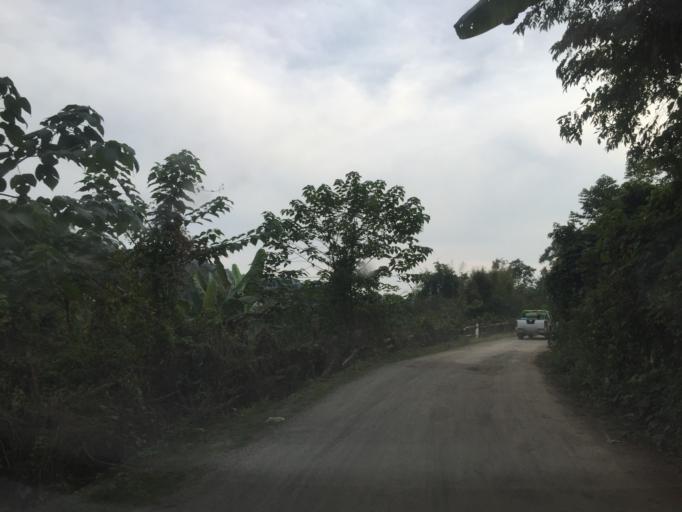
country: TH
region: Chiang Mai
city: Samoeng
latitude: 19.0003
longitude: 98.7289
